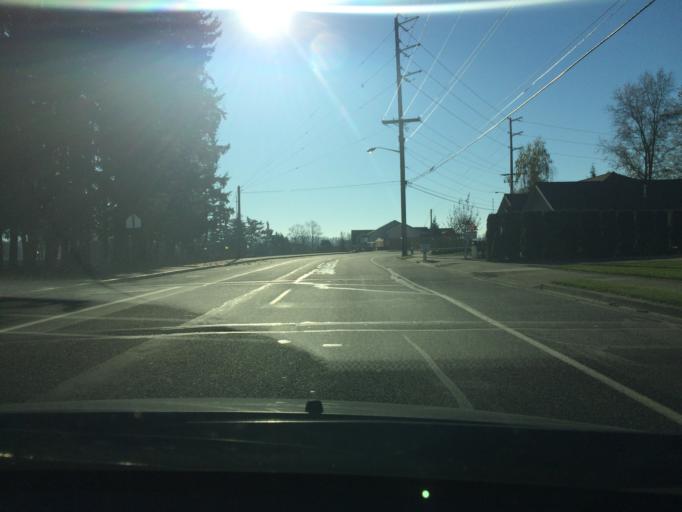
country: US
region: Washington
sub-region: Whatcom County
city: Lynden
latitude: 48.9518
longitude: -122.4300
